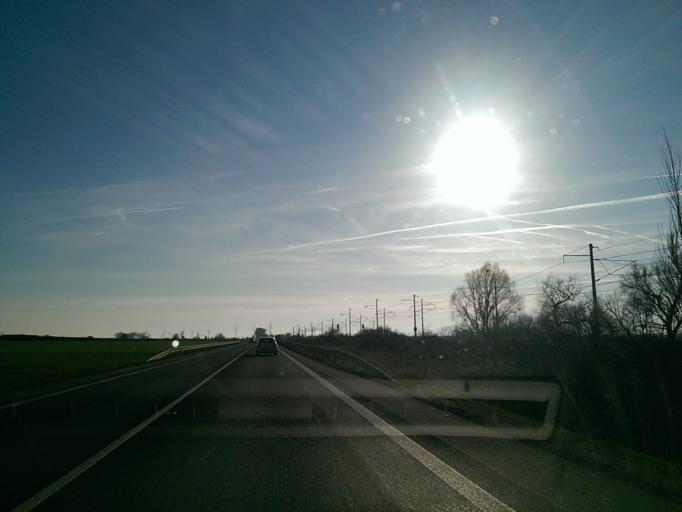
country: CZ
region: Olomoucky
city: Horni Mostenice
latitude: 49.3968
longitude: 17.4537
